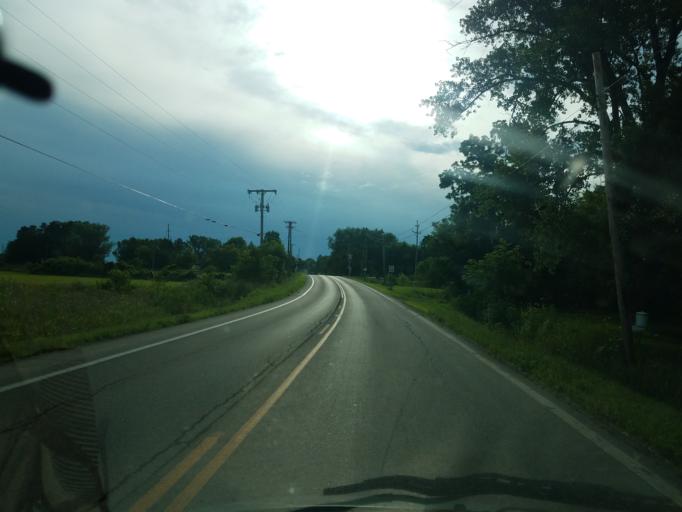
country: US
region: Ohio
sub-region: Ashland County
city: Ashland
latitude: 40.8807
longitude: -82.3516
